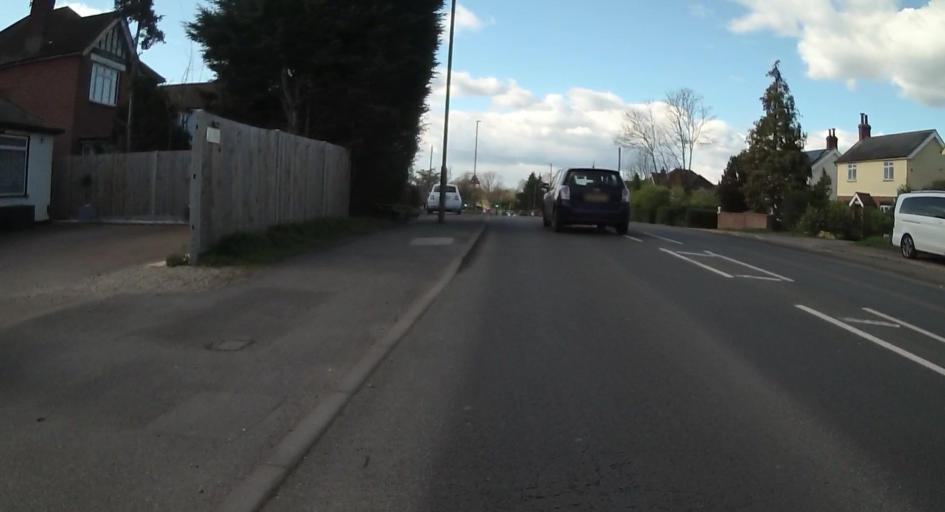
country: GB
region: England
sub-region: Surrey
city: Knaphill
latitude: 51.3216
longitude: -0.6317
